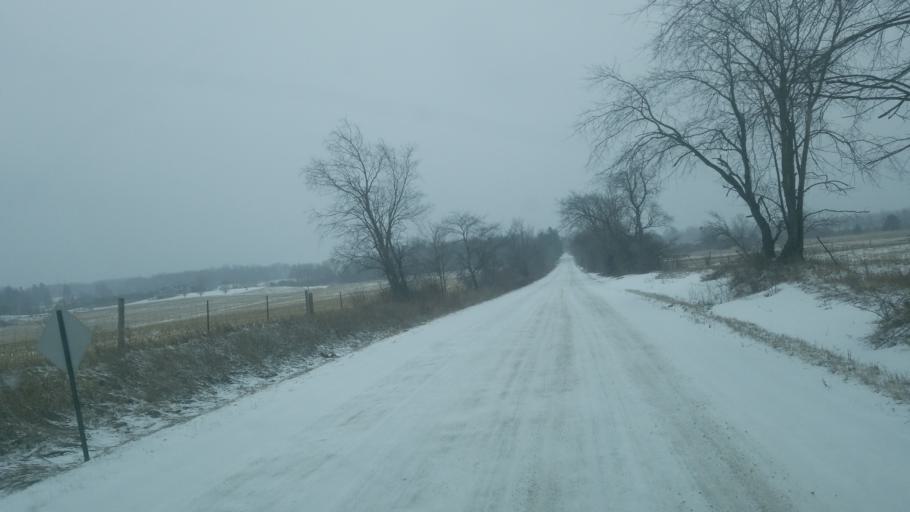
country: US
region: Michigan
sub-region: Osceola County
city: Reed City
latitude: 43.8490
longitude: -85.3939
